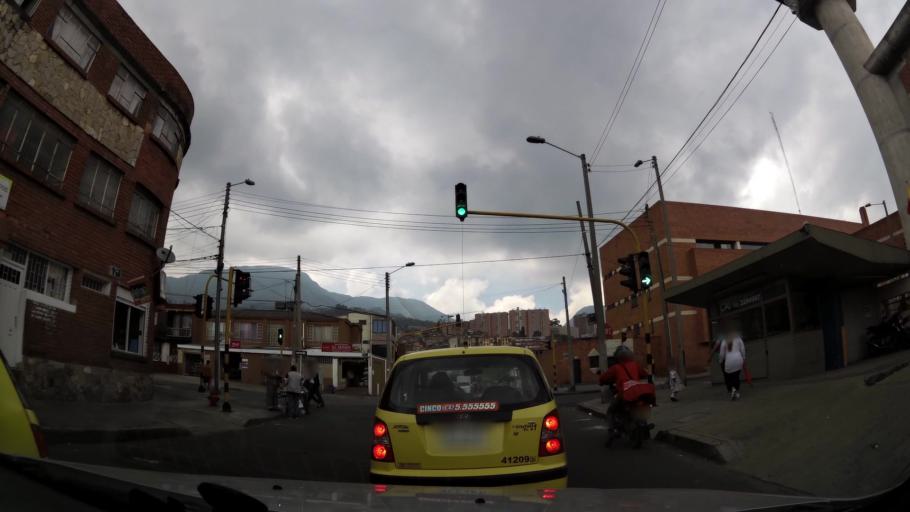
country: CO
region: Bogota D.C.
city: Bogota
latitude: 4.5857
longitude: -74.0846
